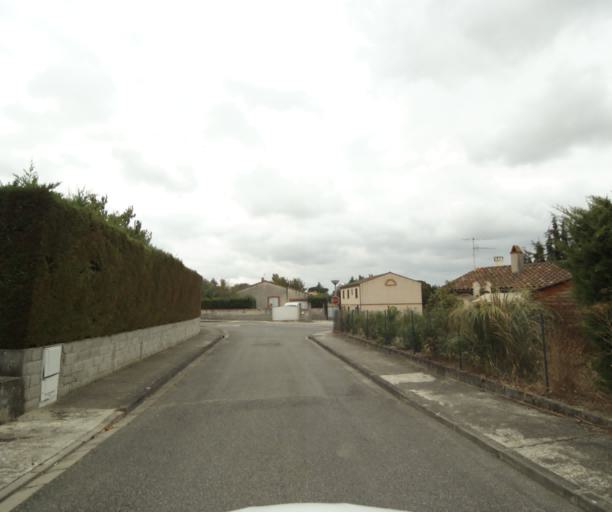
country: FR
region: Midi-Pyrenees
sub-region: Departement de la Haute-Garonne
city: Villefranche-de-Lauragais
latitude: 43.4095
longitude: 1.7146
